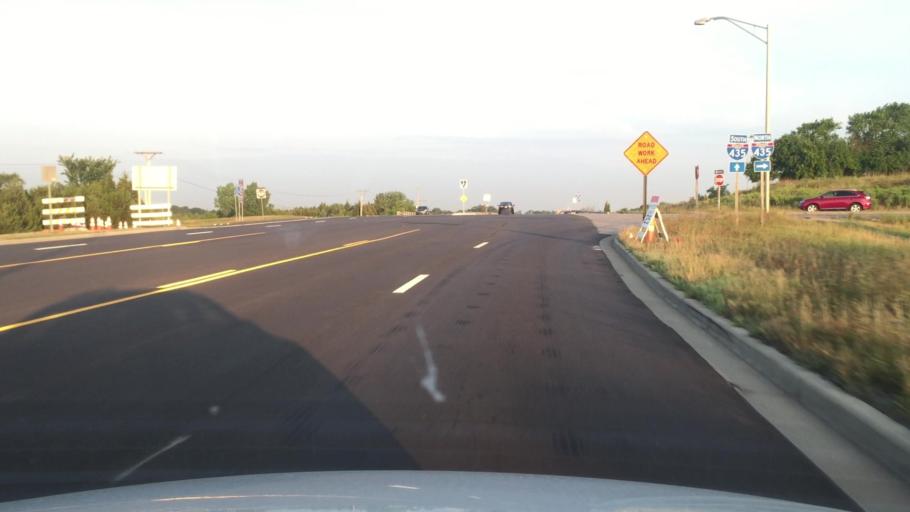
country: US
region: Kansas
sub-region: Wyandotte County
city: Edwardsville
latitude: 39.0220
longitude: -94.7832
